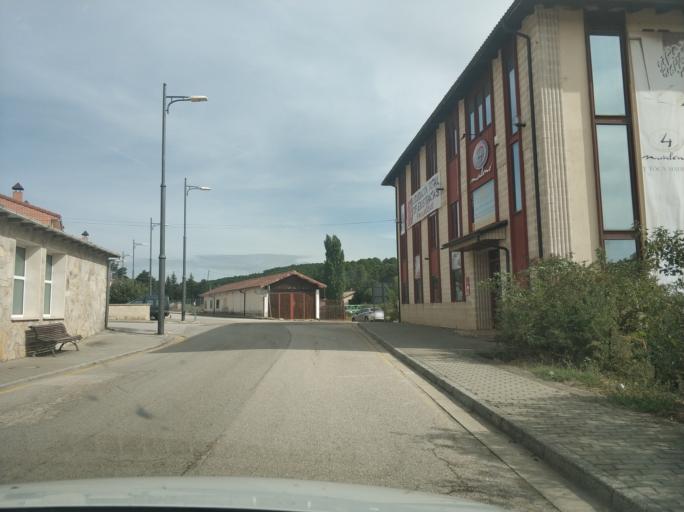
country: ES
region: Castille and Leon
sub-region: Provincia de Soria
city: Navaleno
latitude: 41.8393
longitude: -3.0018
